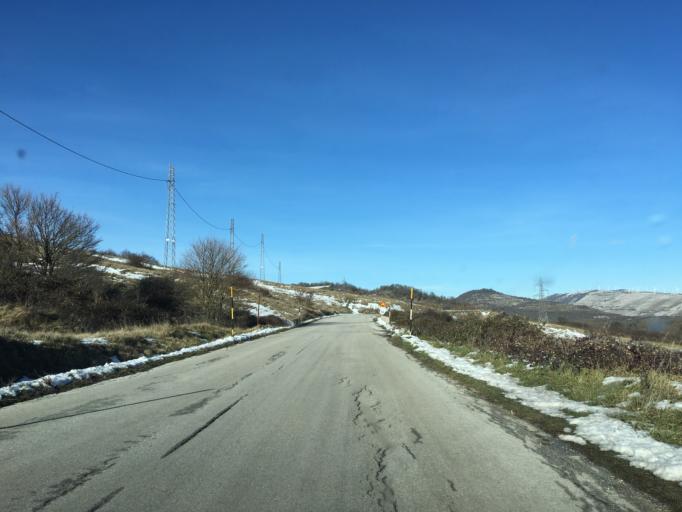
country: IT
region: Abruzzo
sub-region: Provincia di Chieti
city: Rosello
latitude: 41.8574
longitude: 14.3563
